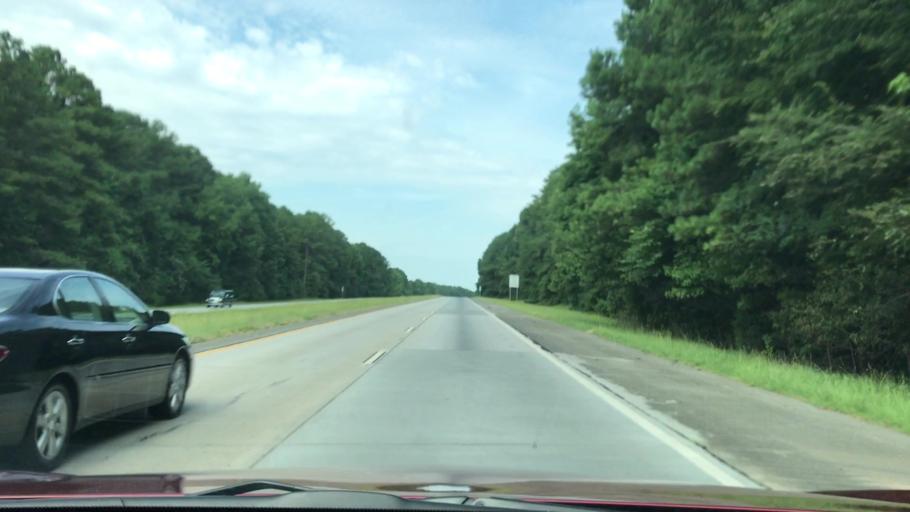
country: US
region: Georgia
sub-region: Warren County
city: Firing Range
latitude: 33.5030
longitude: -82.7726
